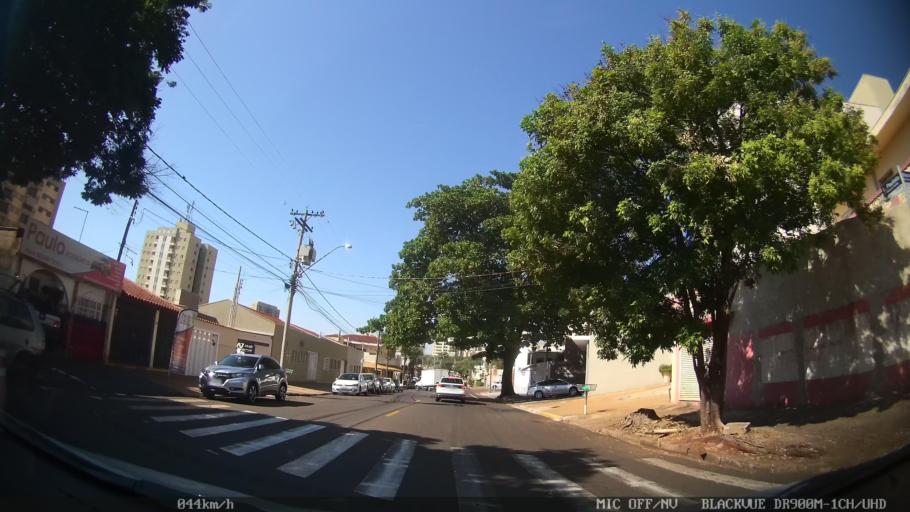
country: BR
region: Sao Paulo
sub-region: Ribeirao Preto
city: Ribeirao Preto
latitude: -21.2047
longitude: -47.7984
